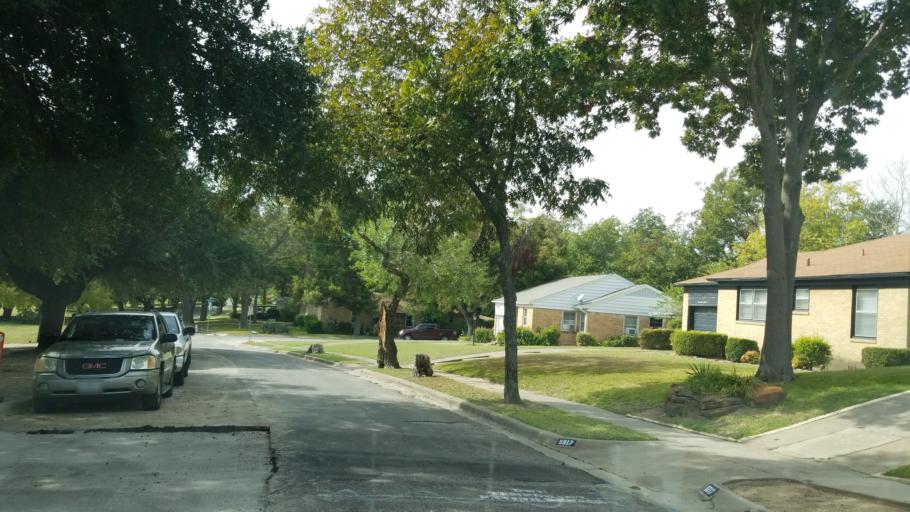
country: US
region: Texas
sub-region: Dallas County
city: Dallas
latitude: 32.7683
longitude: -96.7207
